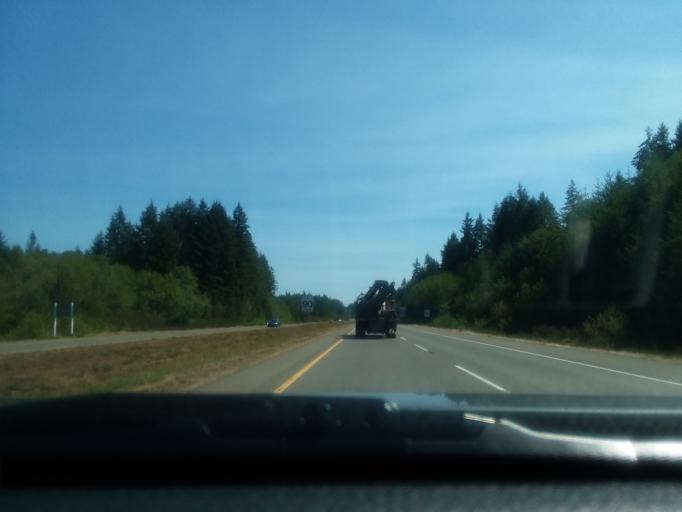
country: CA
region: British Columbia
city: Port Alberni
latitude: 49.4383
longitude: -124.7540
